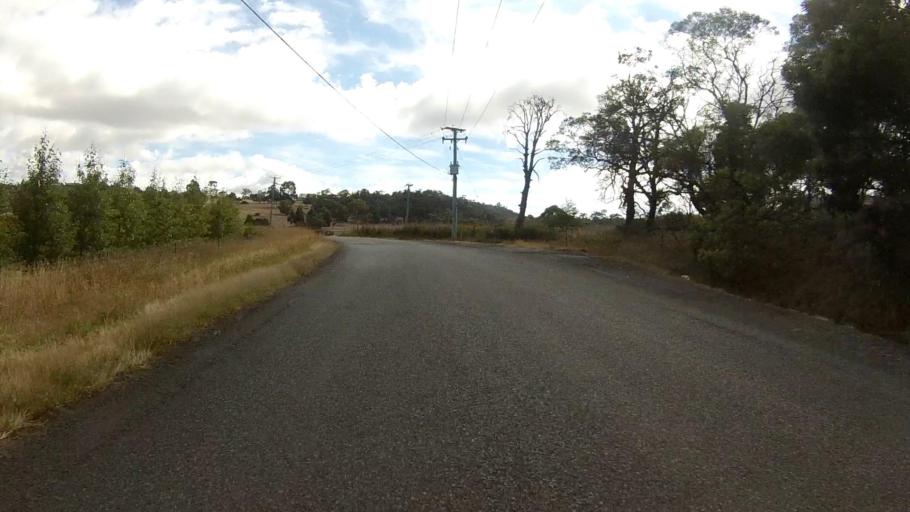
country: AU
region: Tasmania
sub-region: Brighton
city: Old Beach
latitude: -42.7442
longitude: 147.3020
